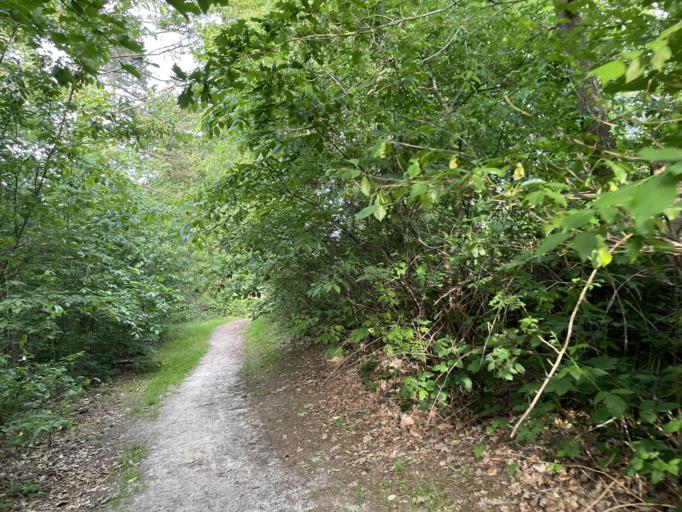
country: DE
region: Schleswig-Holstein
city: Mildstedt
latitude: 54.4653
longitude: 9.1091
